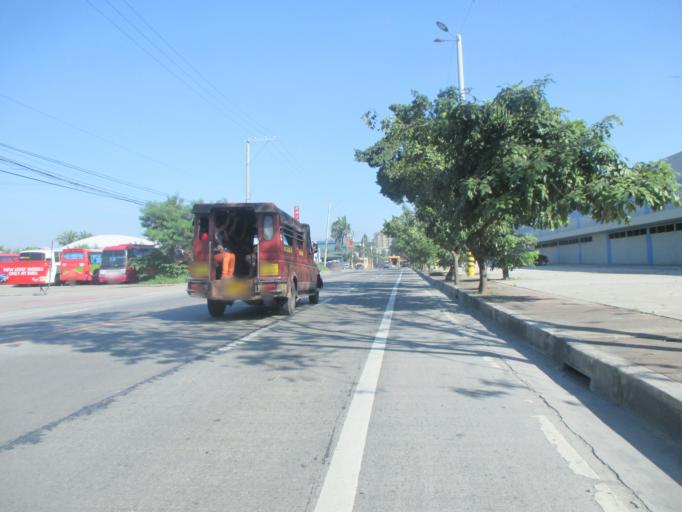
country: PH
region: Metro Manila
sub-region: Marikina
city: Calumpang
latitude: 14.6299
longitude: 121.1019
